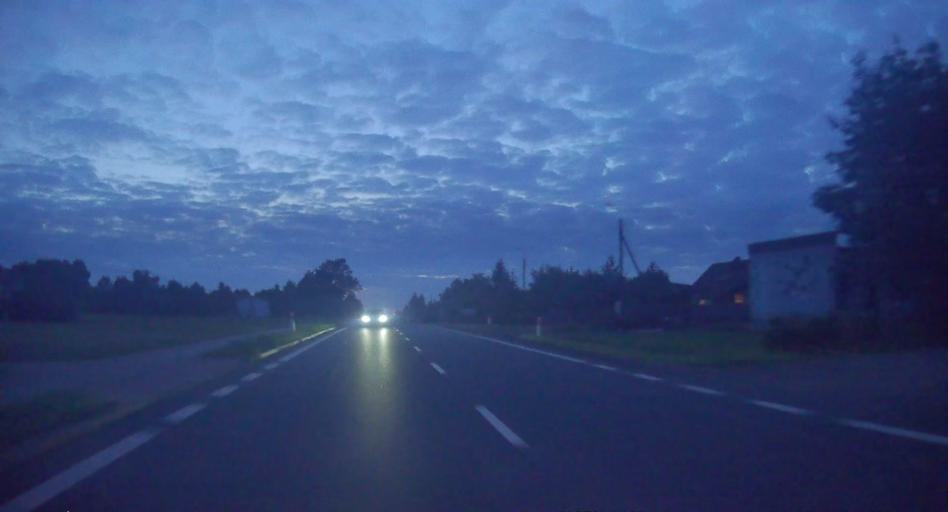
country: PL
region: Silesian Voivodeship
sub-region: Powiat klobucki
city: Kamyk
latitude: 50.8713
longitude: 19.0081
